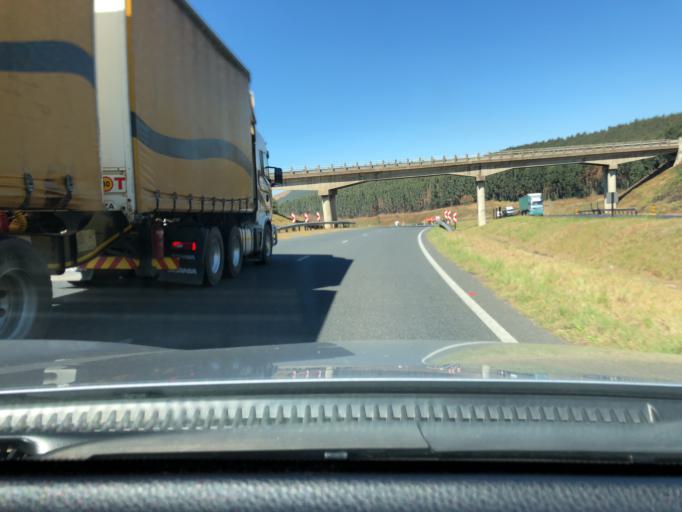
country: ZA
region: KwaZulu-Natal
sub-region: uMgungundlovu District Municipality
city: Howick
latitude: -29.3976
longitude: 30.1382
